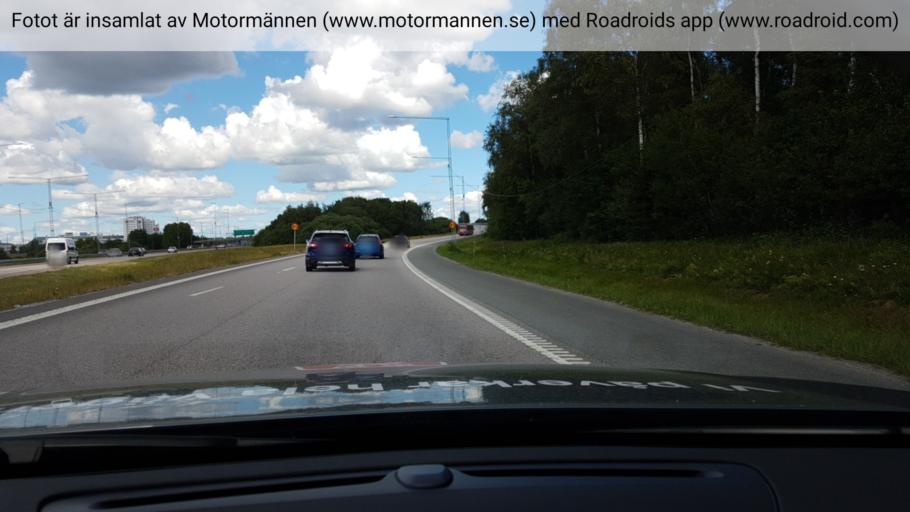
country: SE
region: Stockholm
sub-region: Sigtuna Kommun
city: Rosersberg
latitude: 59.5990
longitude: 17.8973
